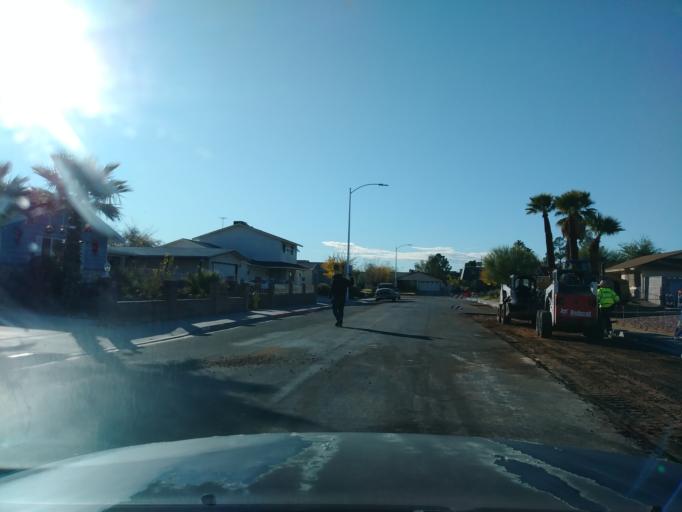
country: US
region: Nevada
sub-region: Clark County
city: Spring Valley
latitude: 36.1615
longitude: -115.2491
